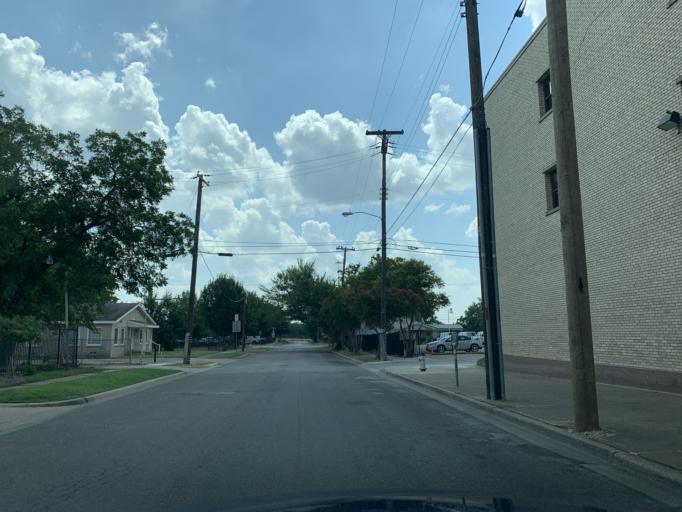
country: US
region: Texas
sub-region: Dallas County
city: Dallas
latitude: 32.7450
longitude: -96.8189
